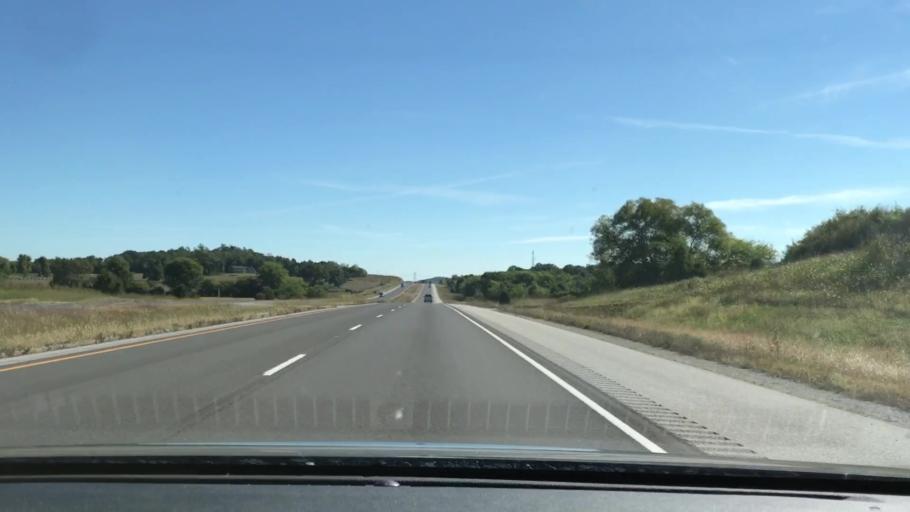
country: US
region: Kentucky
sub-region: Logan County
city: Russellville
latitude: 36.8364
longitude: -86.9473
